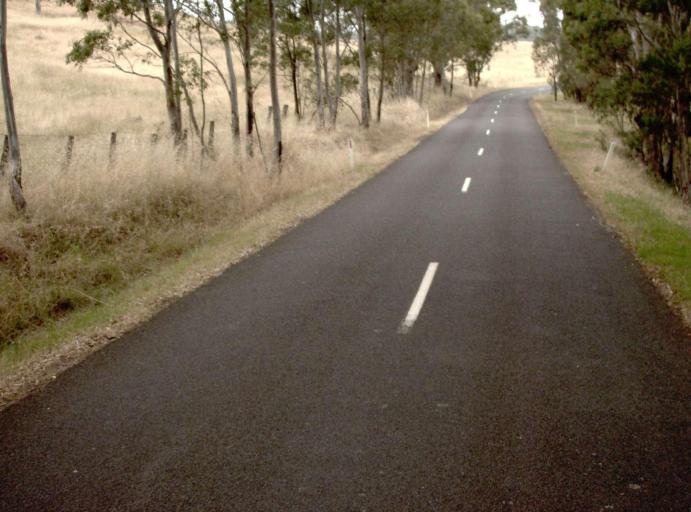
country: AU
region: Victoria
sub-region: Wellington
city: Heyfield
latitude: -37.6826
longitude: 146.6565
